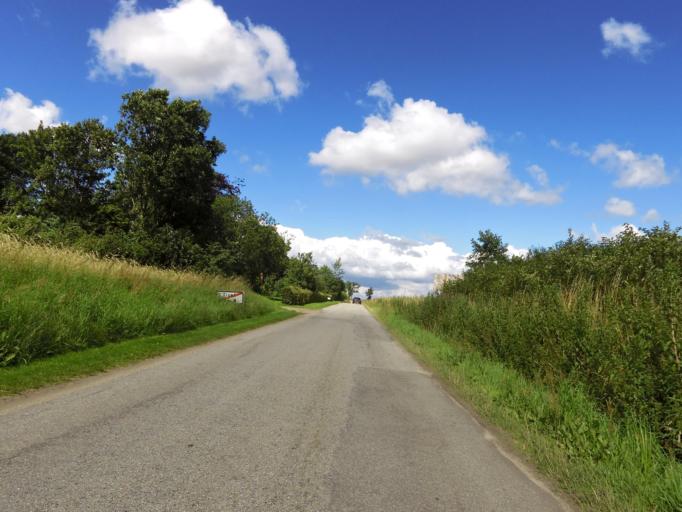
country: DK
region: South Denmark
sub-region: Haderslev Kommune
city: Gram
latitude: 55.2760
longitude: 9.0071
